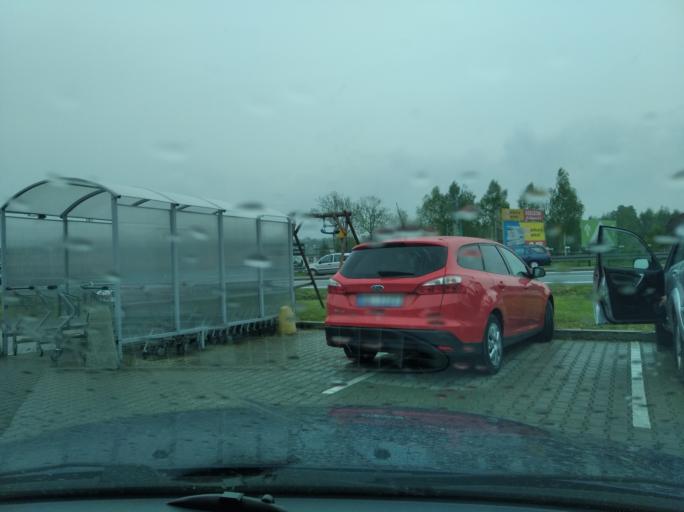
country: PL
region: Subcarpathian Voivodeship
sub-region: Powiat ropczycko-sedziszowski
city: Sedziszow Malopolski
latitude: 50.0643
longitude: 21.7303
